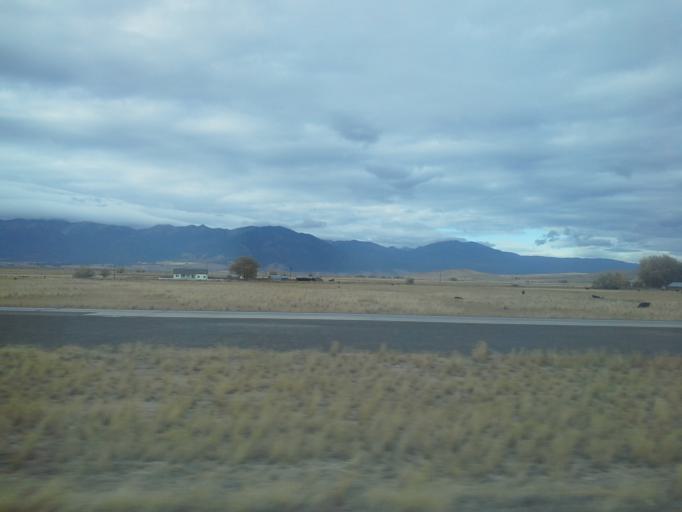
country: US
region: Oregon
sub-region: Baker County
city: Baker City
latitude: 44.8846
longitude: -117.8184
